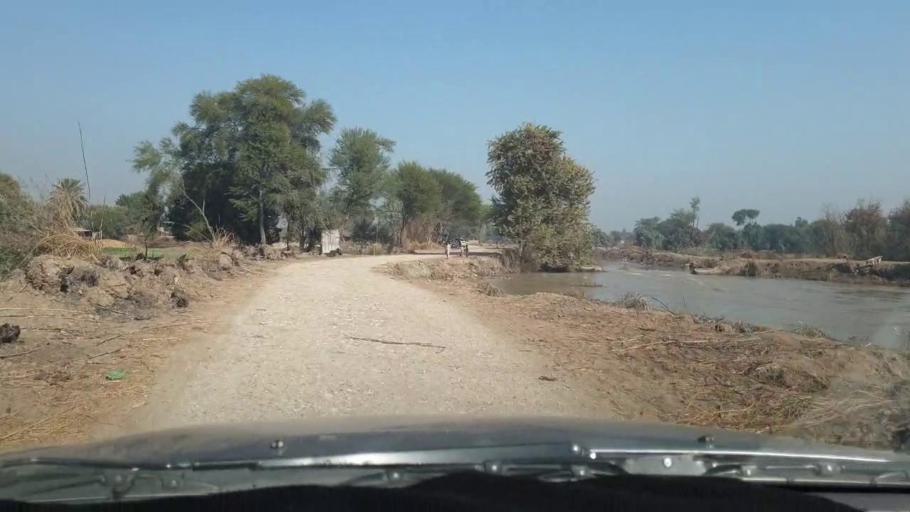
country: PK
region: Sindh
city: Khanpur
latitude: 27.7760
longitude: 69.5380
